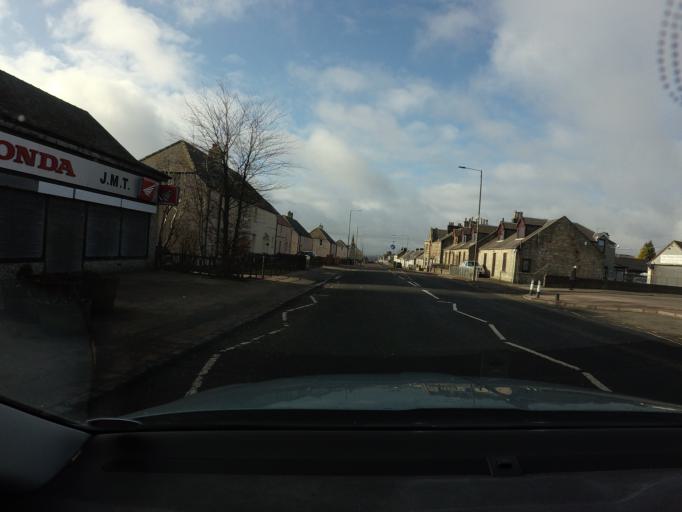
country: GB
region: Scotland
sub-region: South Lanarkshire
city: Forth
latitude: 55.7682
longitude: -3.6860
